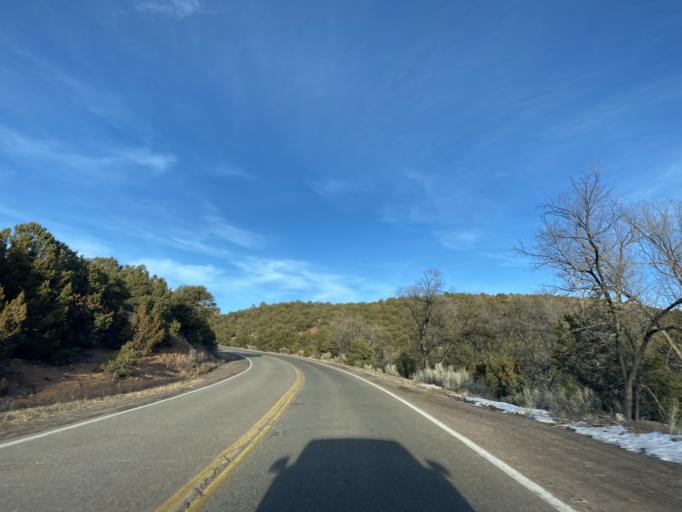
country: US
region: New Mexico
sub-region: Santa Fe County
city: Santa Fe
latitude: 35.7065
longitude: -105.9011
